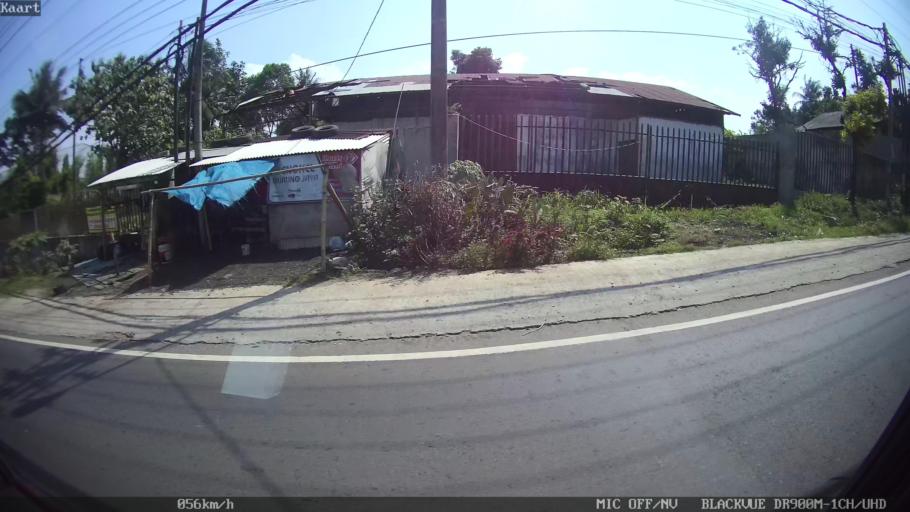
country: ID
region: Lampung
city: Natar
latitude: -5.3460
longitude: 105.2157
